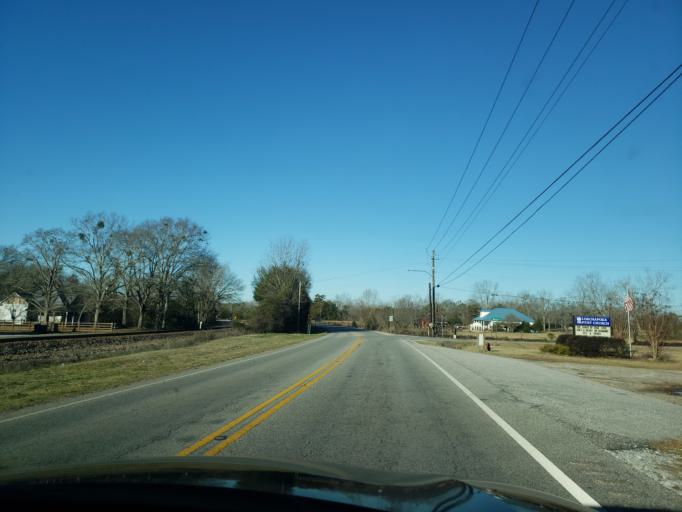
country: US
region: Alabama
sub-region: Lee County
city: Auburn
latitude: 32.6044
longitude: -85.6009
